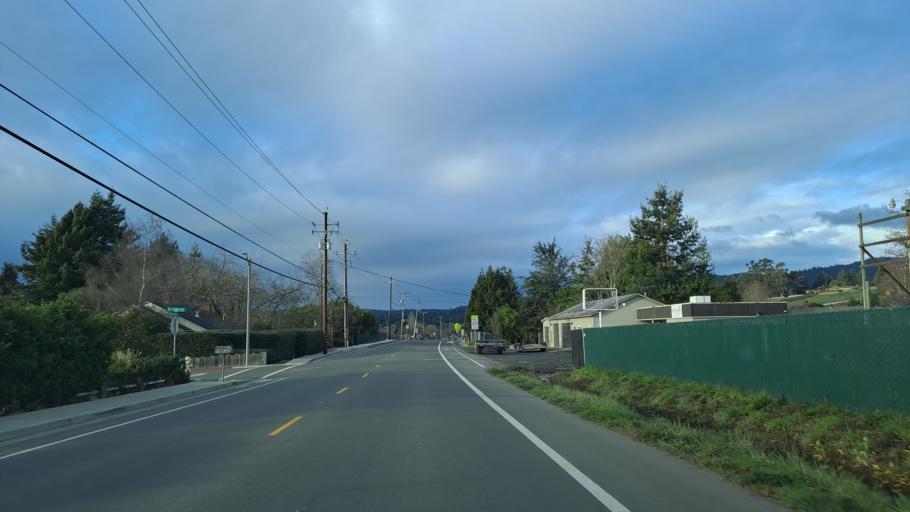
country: US
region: California
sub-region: Humboldt County
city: Fortuna
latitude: 40.5777
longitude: -124.1295
